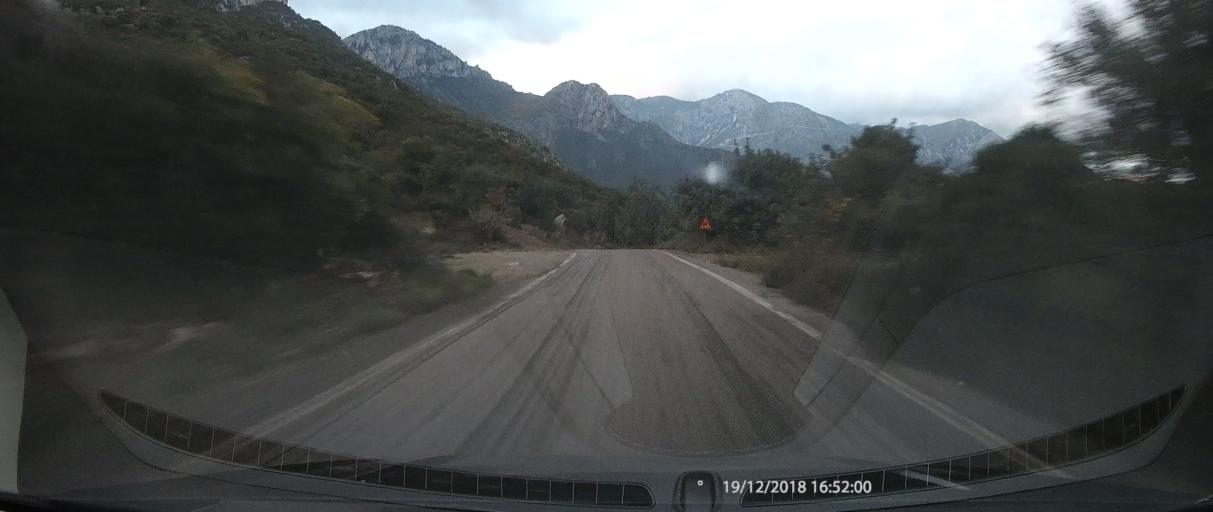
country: GR
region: Peloponnese
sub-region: Nomos Lakonias
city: Sykea
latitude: 36.9543
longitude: 22.9926
